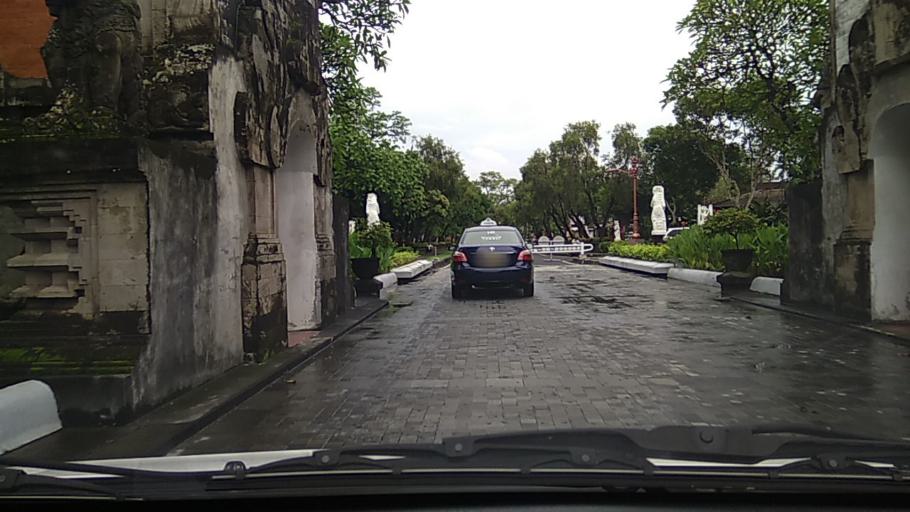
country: ID
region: Bali
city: Bualu
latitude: -8.7977
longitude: 115.2255
